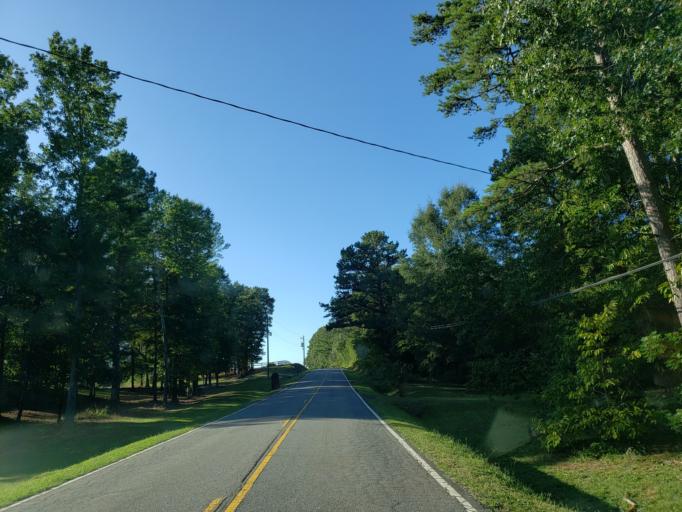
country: US
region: Georgia
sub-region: Bartow County
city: Rydal
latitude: 34.3178
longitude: -84.7610
